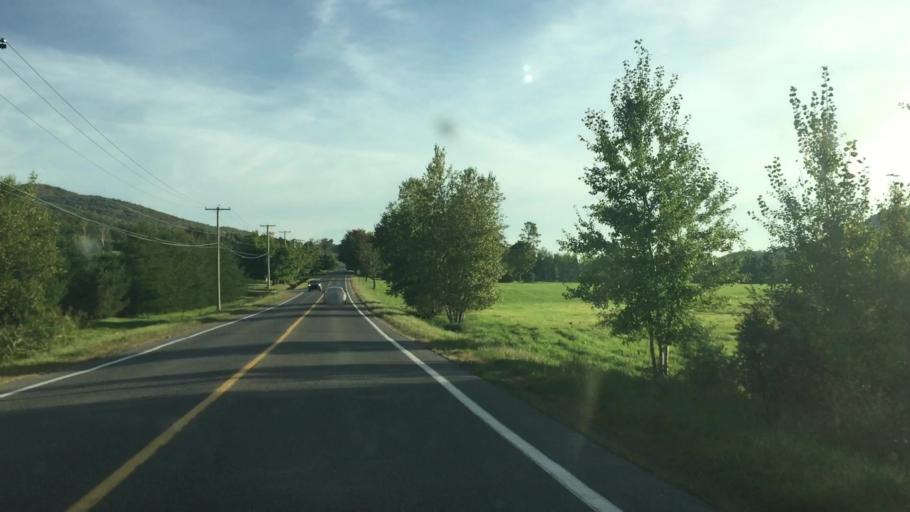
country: CA
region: Quebec
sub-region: Monteregie
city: Bromont
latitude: 45.3049
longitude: -72.6591
